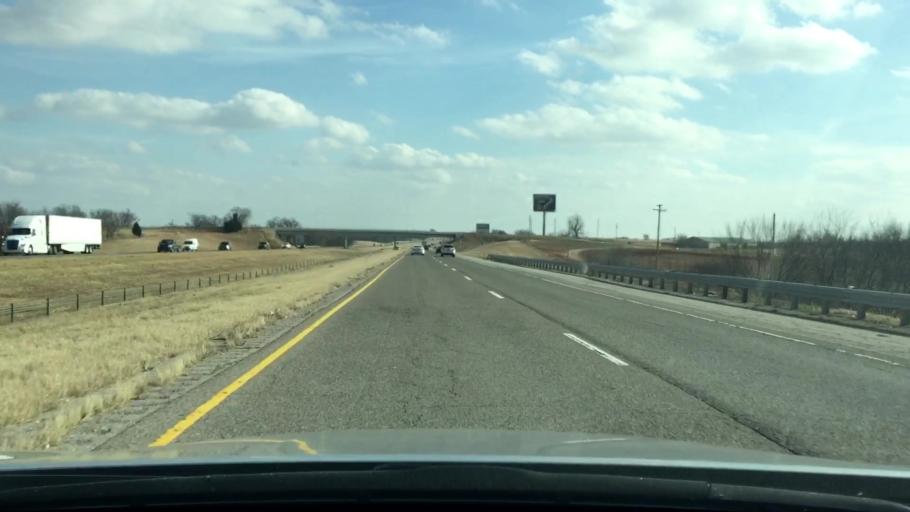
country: US
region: Oklahoma
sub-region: Garvin County
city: Maysville
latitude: 34.8987
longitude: -97.3469
